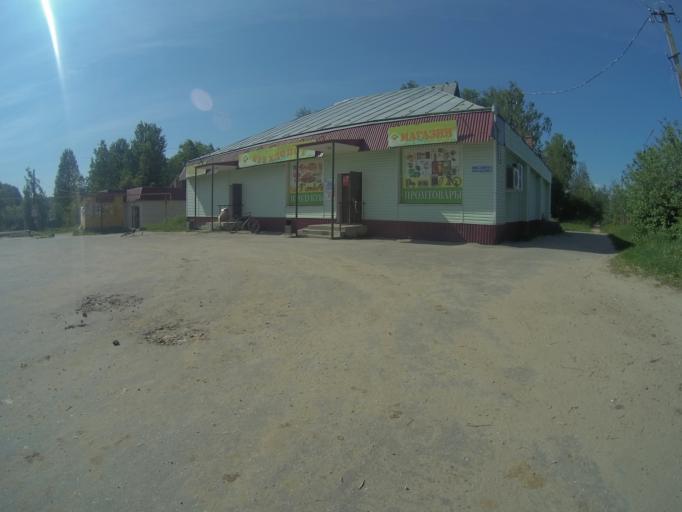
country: RU
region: Vladimir
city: Stavrovo
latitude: 56.1456
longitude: 40.0445
